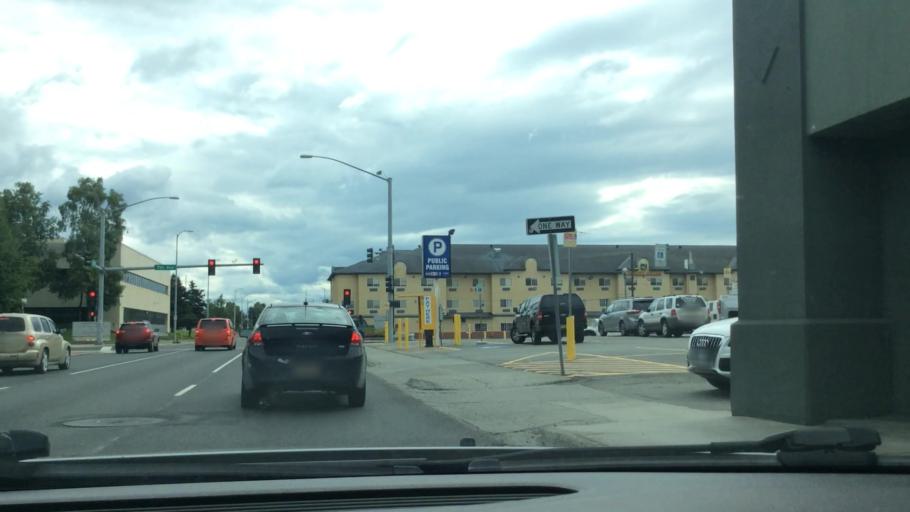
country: US
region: Alaska
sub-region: Anchorage Municipality
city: Anchorage
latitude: 61.2162
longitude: -149.8874
